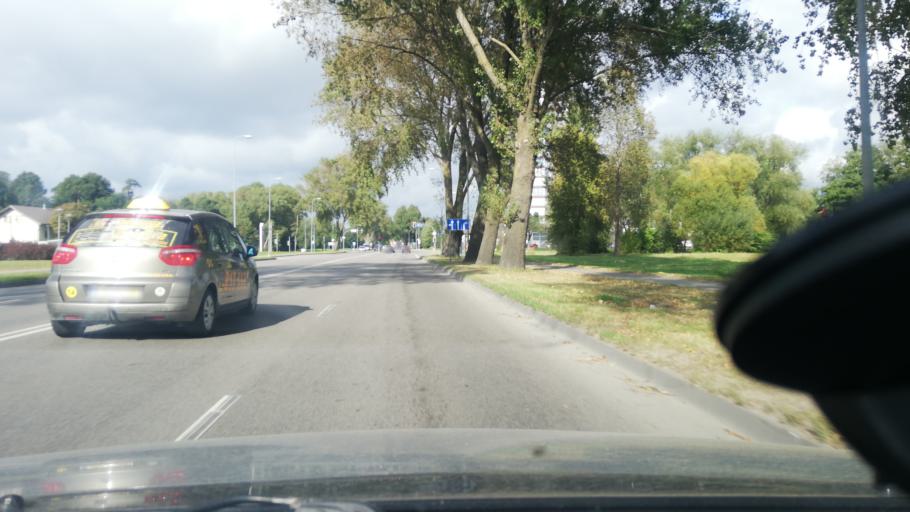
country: LT
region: Klaipedos apskritis
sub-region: Klaipeda
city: Klaipeda
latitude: 55.6694
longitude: 21.1599
